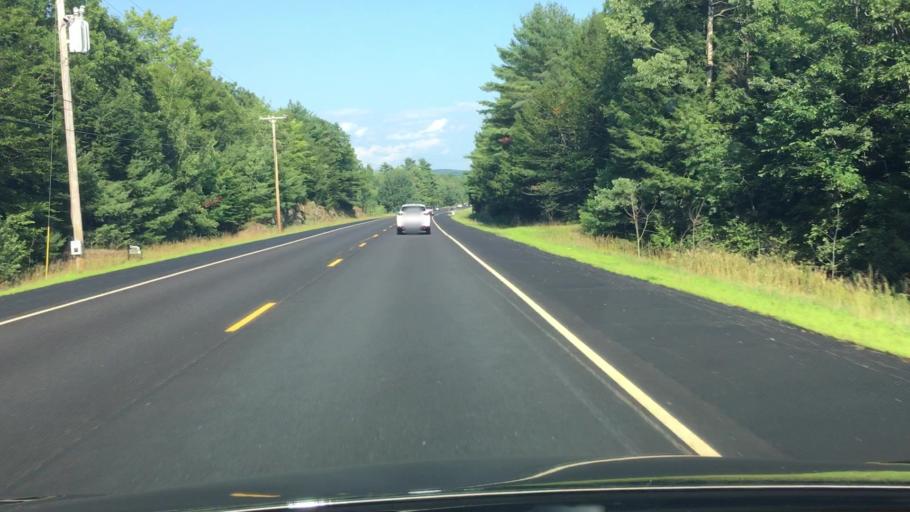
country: US
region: Maine
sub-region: Waldo County
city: Palermo
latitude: 44.4105
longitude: -69.5021
